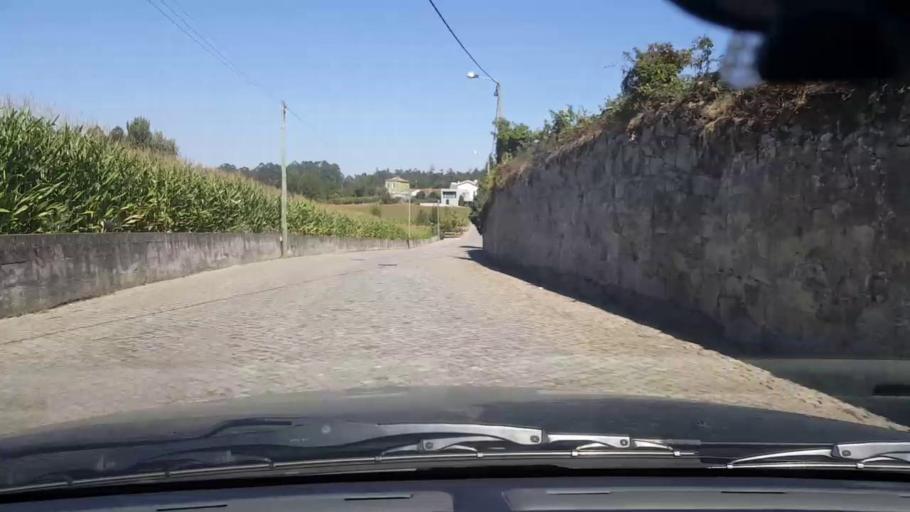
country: PT
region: Porto
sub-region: Matosinhos
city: Lavra
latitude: 41.2699
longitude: -8.6950
